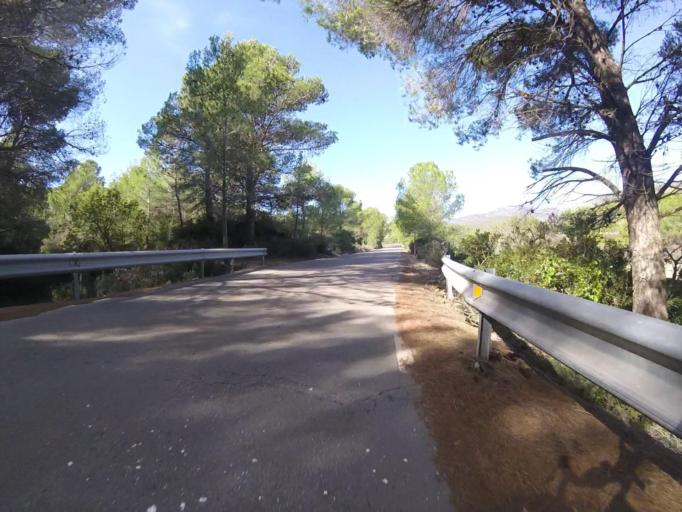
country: ES
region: Valencia
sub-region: Provincia de Castello
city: Sarratella
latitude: 40.2715
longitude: 0.0414
